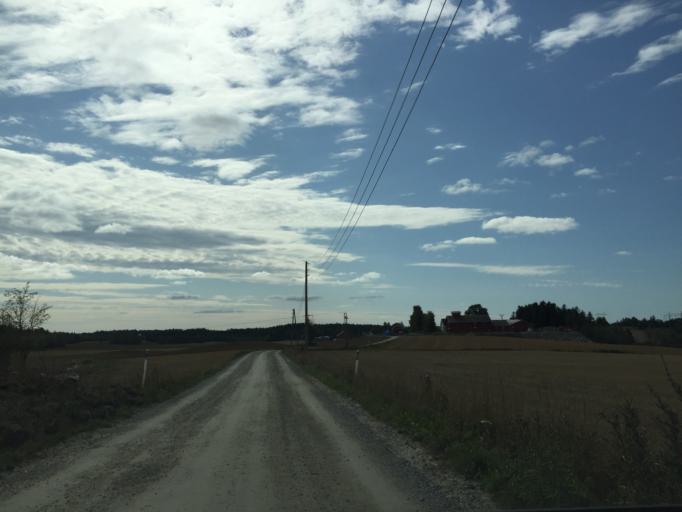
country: NO
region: Ostfold
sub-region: Hobol
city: Elvestad
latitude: 59.6407
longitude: 10.8881
